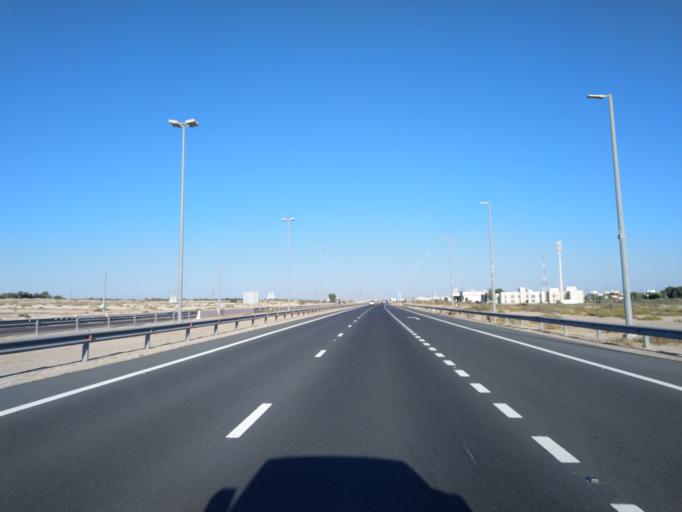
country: OM
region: Al Buraimi
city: Al Buraymi
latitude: 24.5167
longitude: 55.5023
